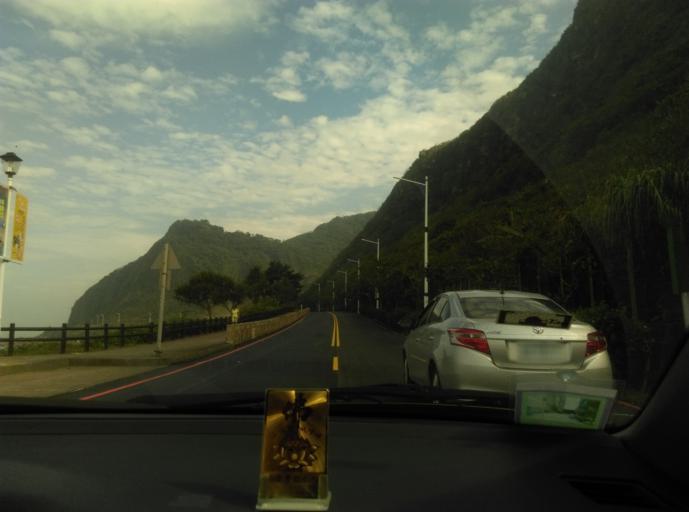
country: TW
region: Taiwan
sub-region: Keelung
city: Keelung
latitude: 25.1644
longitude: 121.7082
